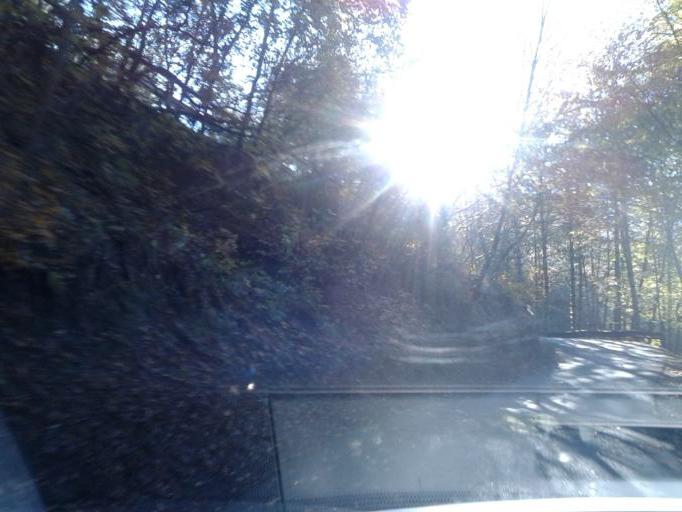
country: IT
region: Trentino-Alto Adige
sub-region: Provincia di Trento
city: Storo
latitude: 45.8491
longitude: 10.5883
